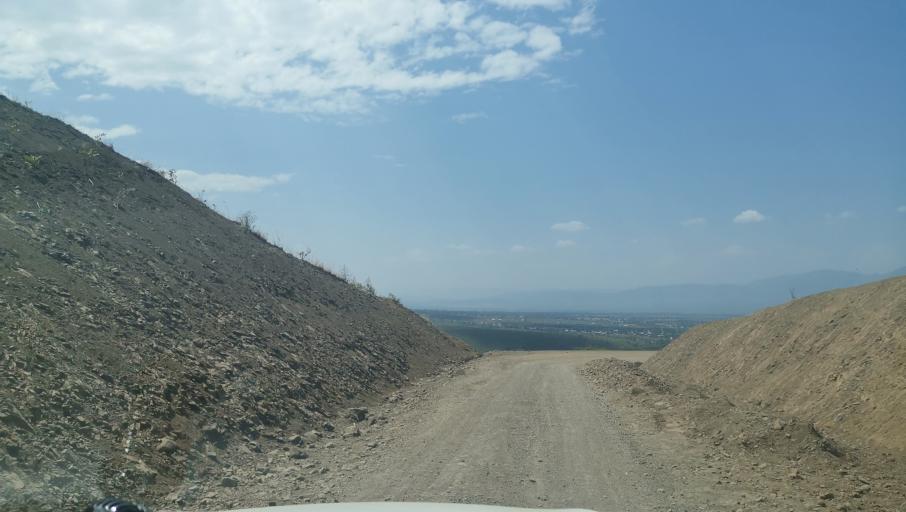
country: ET
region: Southern Nations, Nationalities, and People's Region
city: Arba Minch'
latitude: 6.3342
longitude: 37.3302
